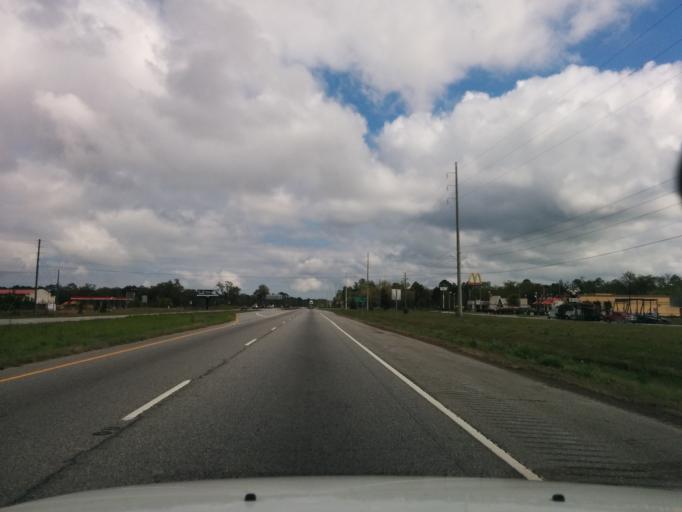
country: US
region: Georgia
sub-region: Glynn County
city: Brunswick
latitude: 31.1354
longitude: -81.5697
